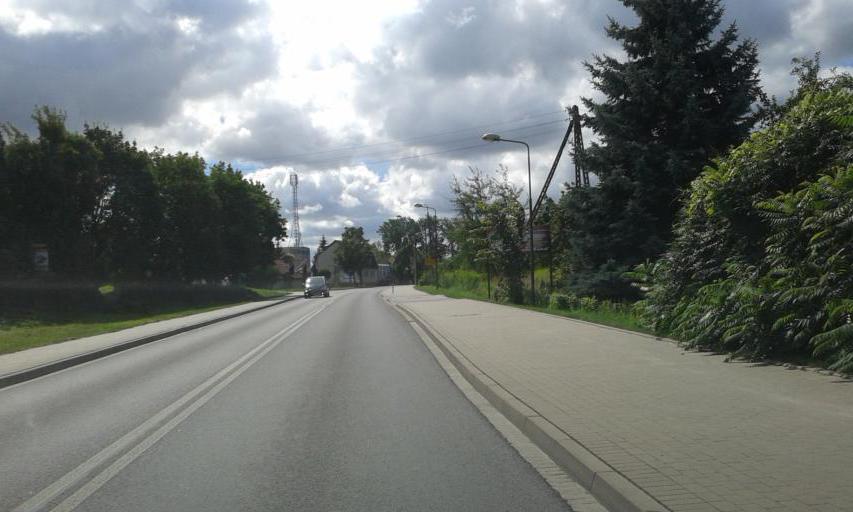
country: PL
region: West Pomeranian Voivodeship
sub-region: Powiat walecki
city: Walcz
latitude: 53.2809
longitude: 16.4633
